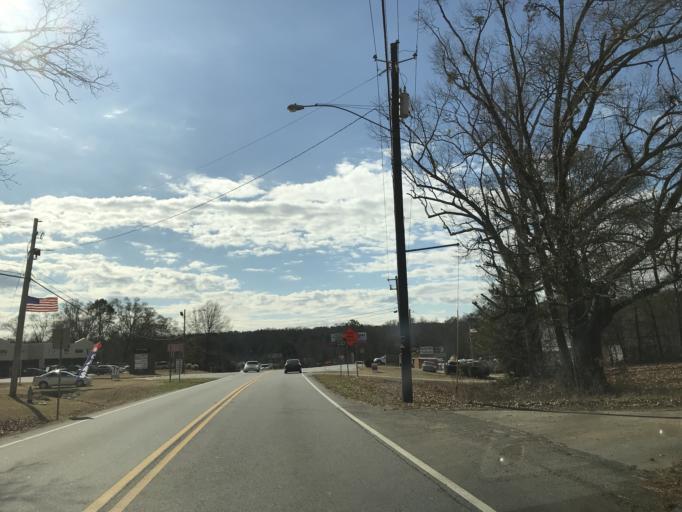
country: US
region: Georgia
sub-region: Paulding County
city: Hiram
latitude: 33.8733
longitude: -84.7634
